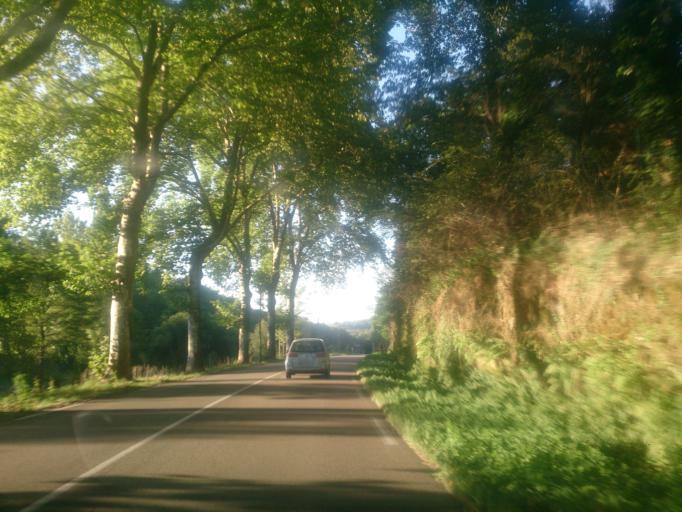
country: FR
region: Limousin
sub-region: Departement de la Correze
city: Brive-la-Gaillarde
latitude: 45.1236
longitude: 1.5173
